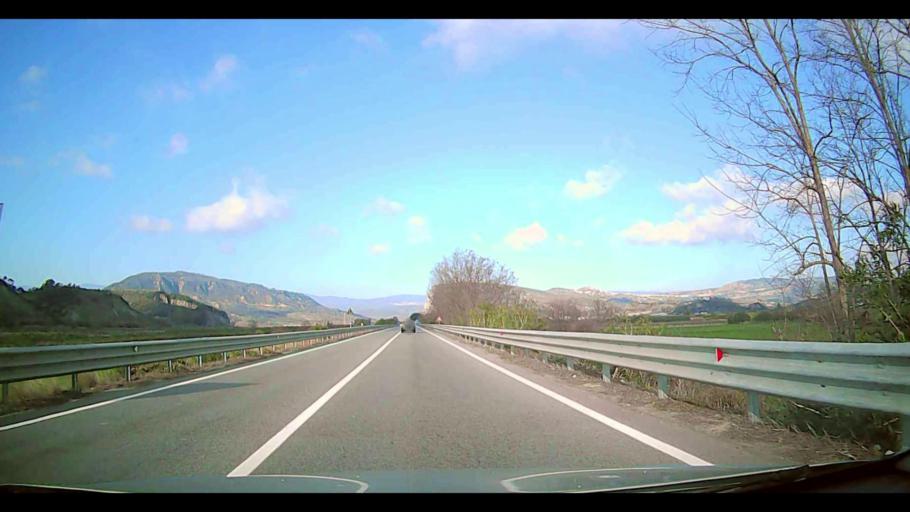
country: IT
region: Calabria
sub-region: Provincia di Crotone
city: Santa Severina
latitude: 39.1765
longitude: 16.9296
